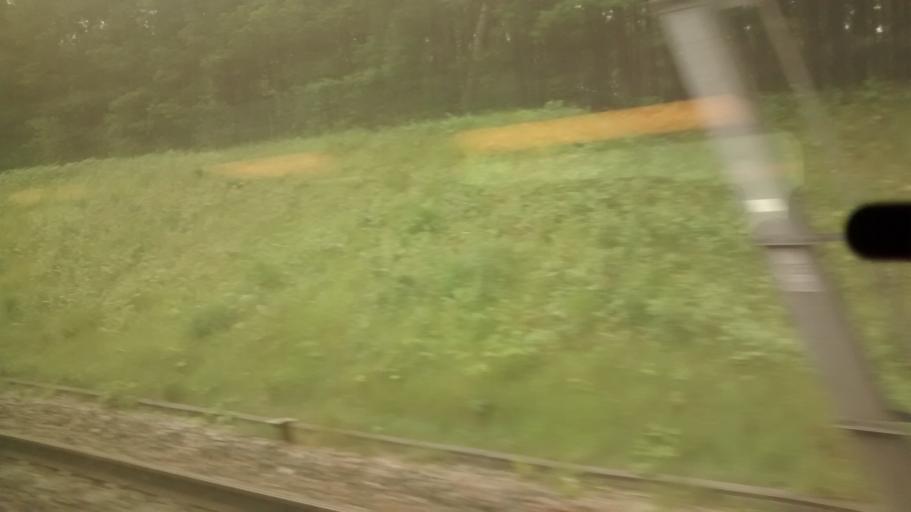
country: FR
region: Ile-de-France
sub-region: Departement de l'Essonne
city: Yerres
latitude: 48.7339
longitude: 2.5017
